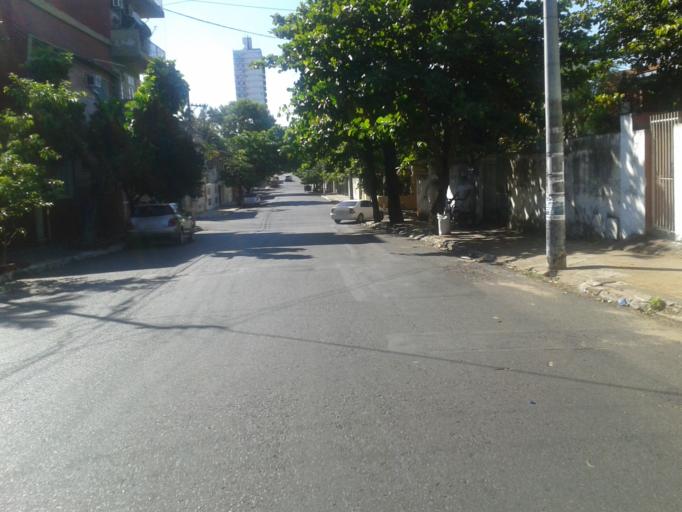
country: PY
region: Asuncion
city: Asuncion
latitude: -25.2916
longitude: -57.6435
